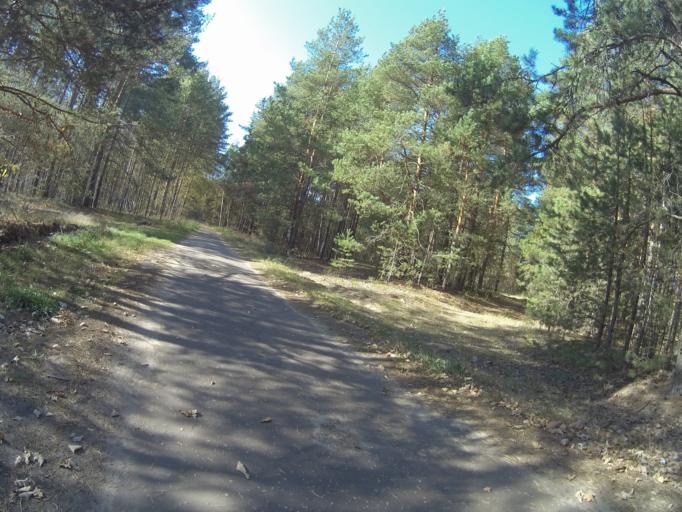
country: RU
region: Vladimir
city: Raduzhnyy
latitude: 56.0377
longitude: 40.3692
